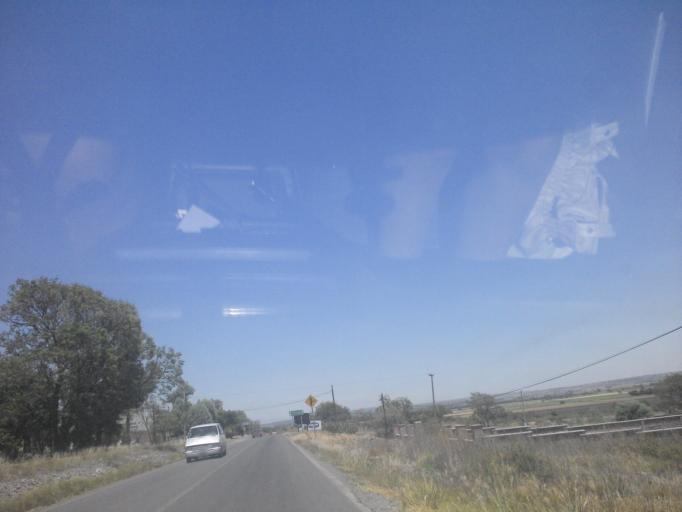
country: MX
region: Guanajuato
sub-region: San Francisco del Rincon
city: San Ignacio de Hidalgo
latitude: 20.8963
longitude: -101.9244
